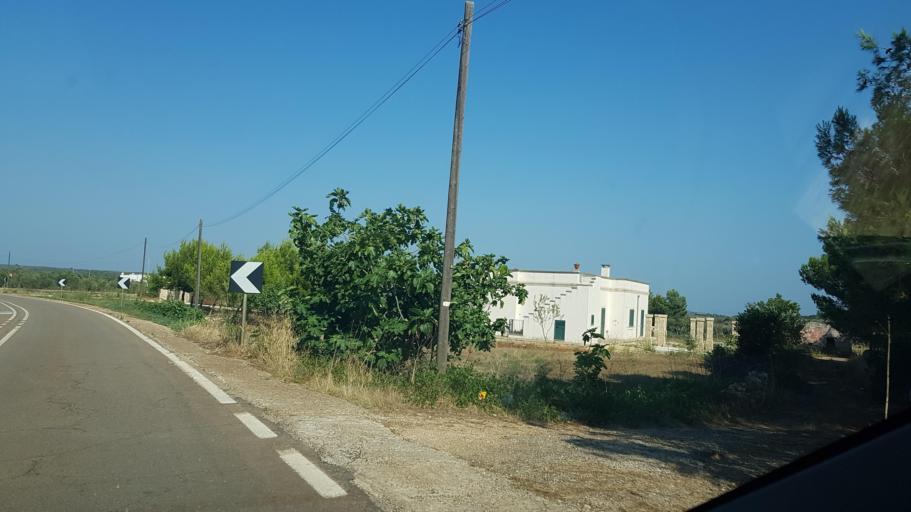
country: IT
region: Apulia
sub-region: Provincia di Lecce
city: Gemini
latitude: 39.8669
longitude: 18.2148
